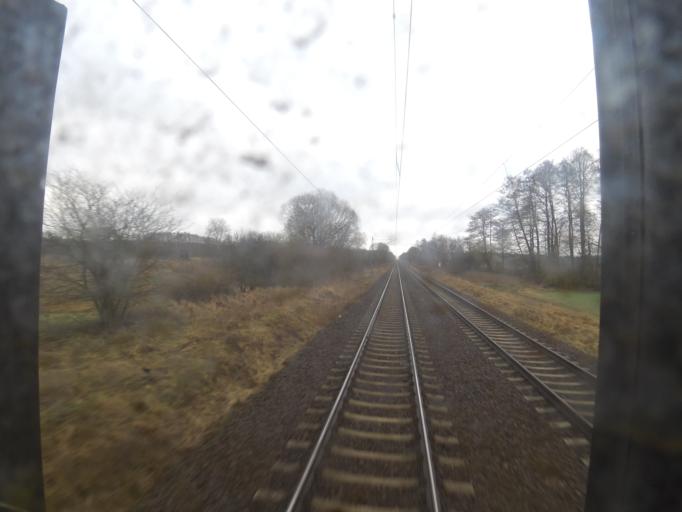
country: DE
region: Brandenburg
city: Zossen
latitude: 52.1966
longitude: 13.4476
